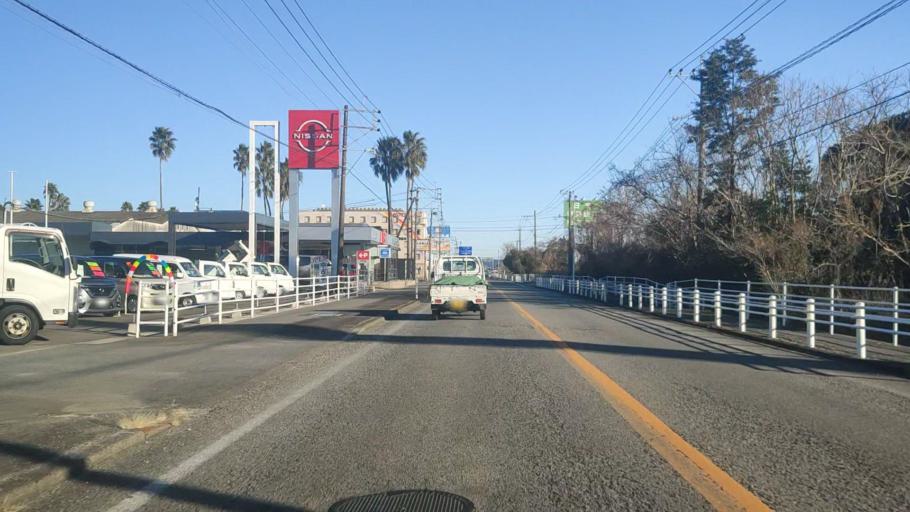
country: JP
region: Miyazaki
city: Nobeoka
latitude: 32.3924
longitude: 131.6281
